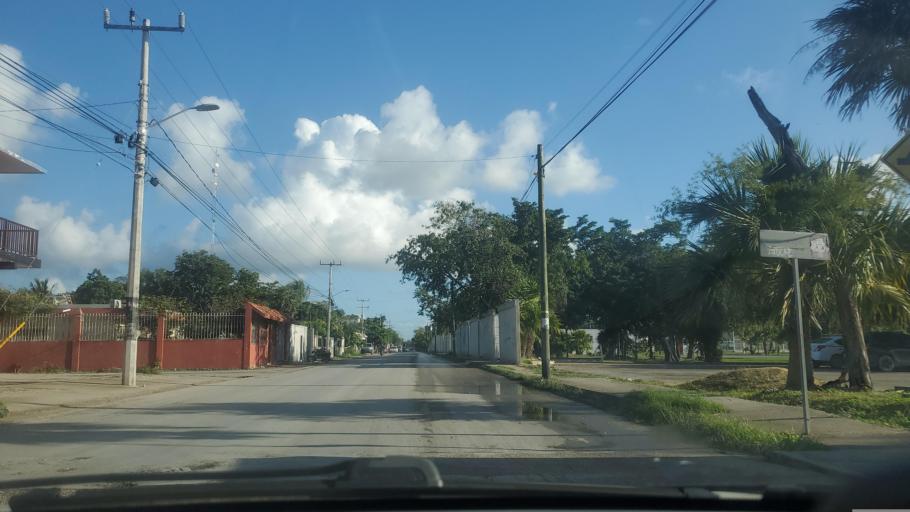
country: MX
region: Quintana Roo
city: Tulum
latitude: 20.2117
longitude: -87.4693
